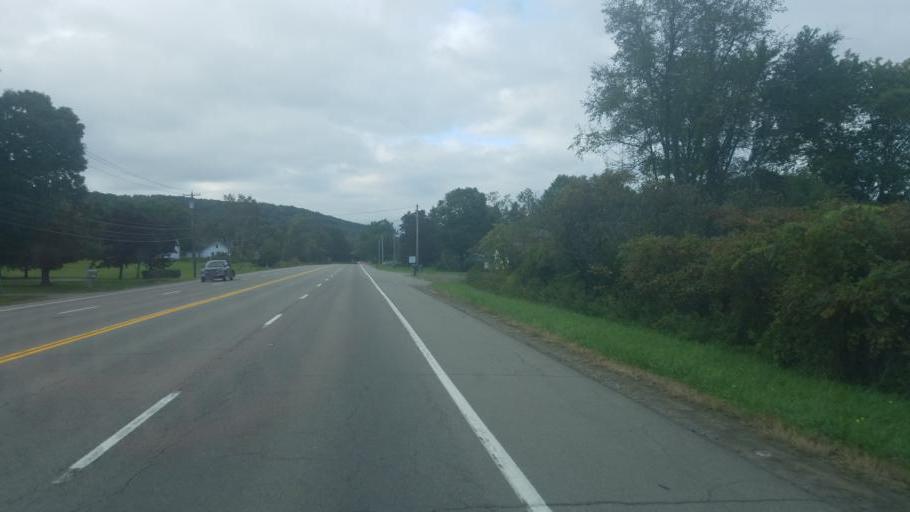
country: US
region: New York
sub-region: Cattaraugus County
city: Olean
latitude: 42.1420
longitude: -78.4006
